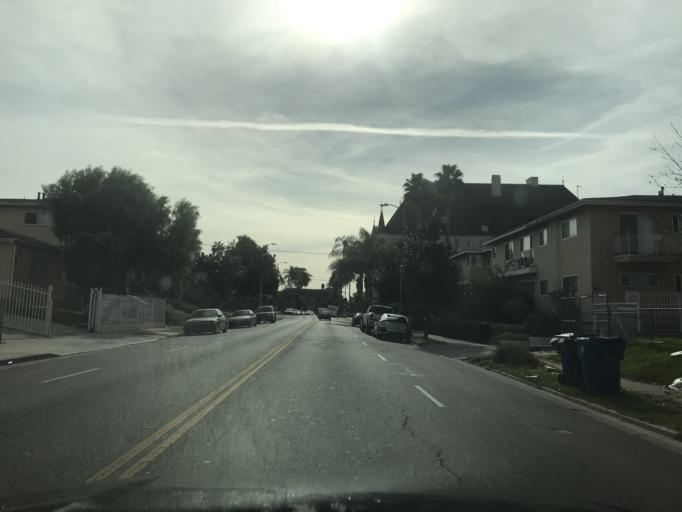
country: US
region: California
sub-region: Los Angeles County
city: Hollywood
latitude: 34.0664
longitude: -118.3141
